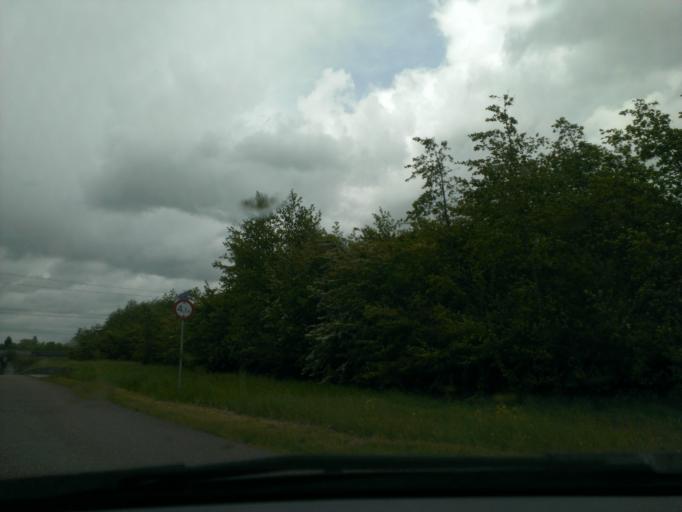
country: NL
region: Gelderland
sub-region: Gemeente Westervoort
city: Westervoort
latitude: 51.9025
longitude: 5.9391
